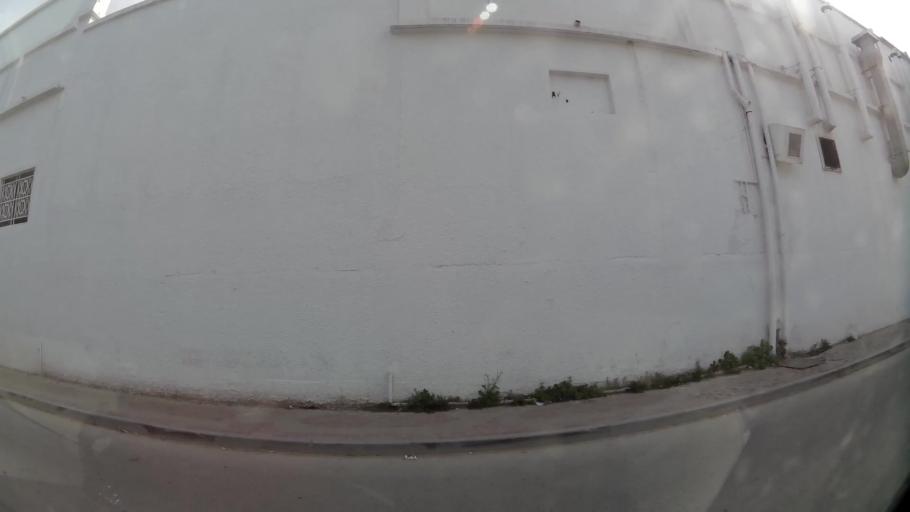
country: QA
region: Baladiyat ad Dawhah
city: Doha
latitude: 25.2868
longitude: 51.5214
